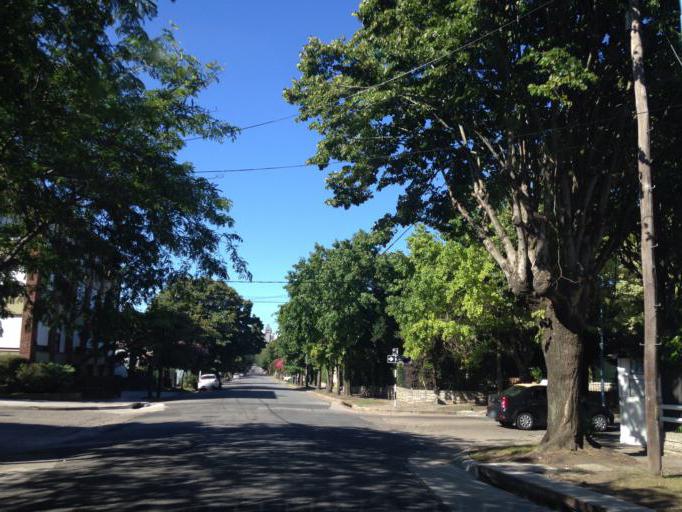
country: AR
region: Buenos Aires
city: Mar del Plata
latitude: -38.0215
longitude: -57.5421
